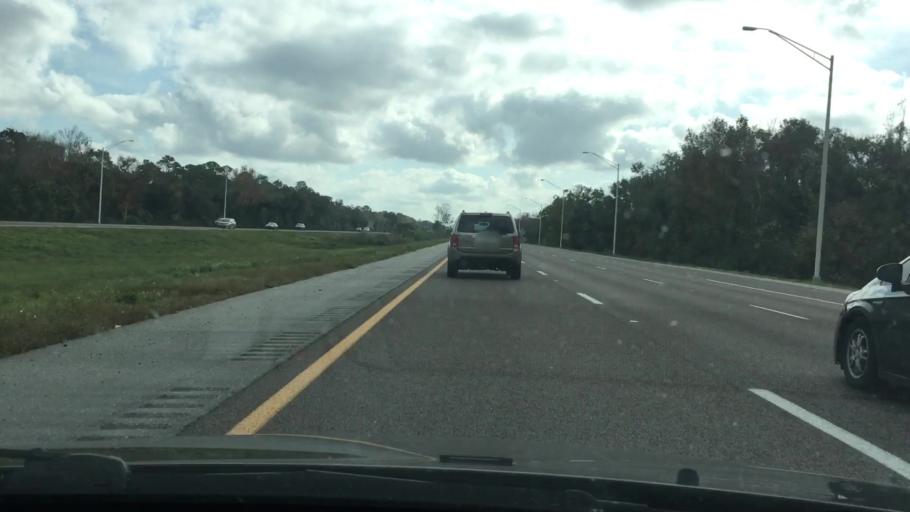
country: US
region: Florida
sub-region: Volusia County
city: Edgewater
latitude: 28.9463
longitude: -80.9489
